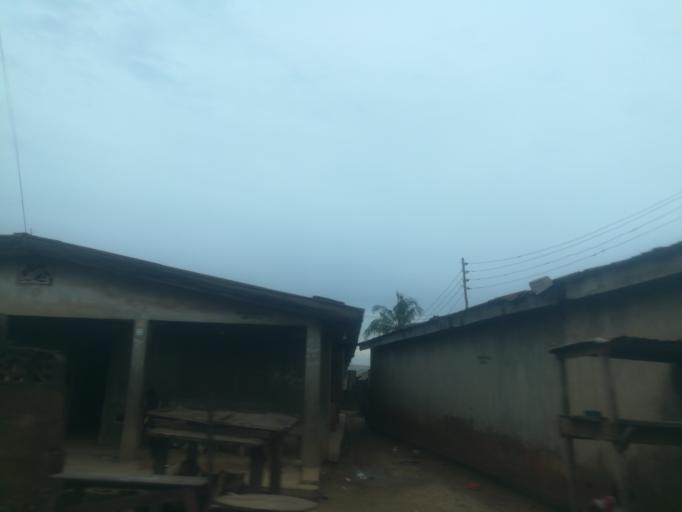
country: NG
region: Oyo
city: Egbeda
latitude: 7.4003
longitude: 3.9786
